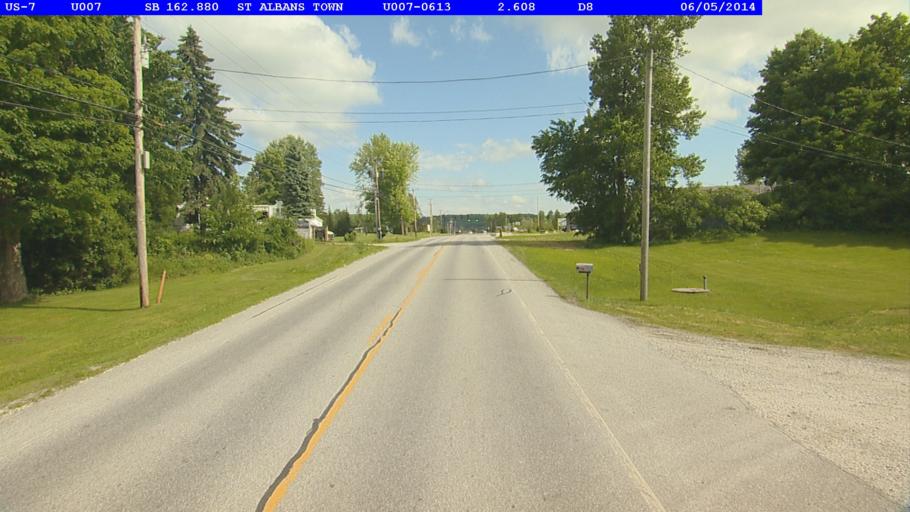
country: US
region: Vermont
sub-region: Franklin County
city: Saint Albans
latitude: 44.8452
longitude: -73.0863
